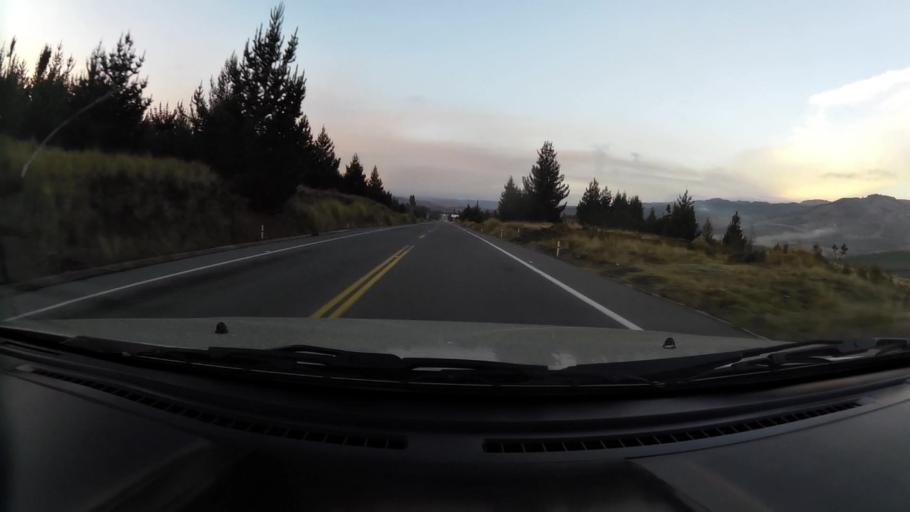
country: EC
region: Chimborazo
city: Alausi
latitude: -2.0388
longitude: -78.7370
